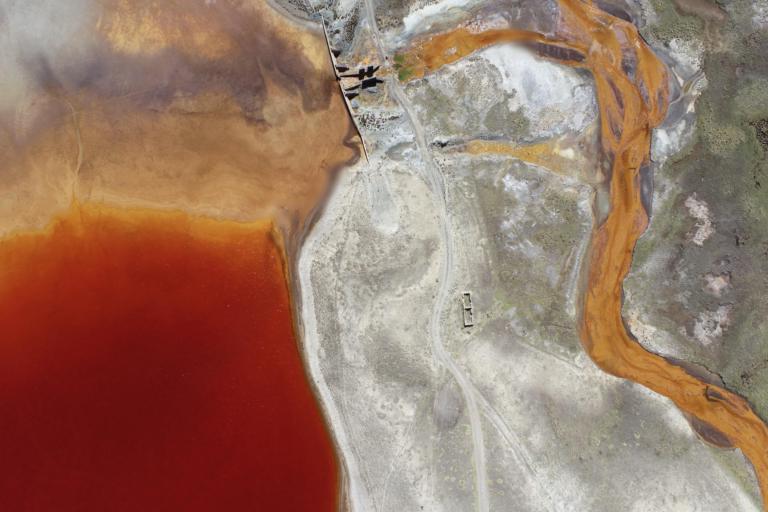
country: BO
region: La Paz
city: La Paz
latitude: -16.3418
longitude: -68.1596
